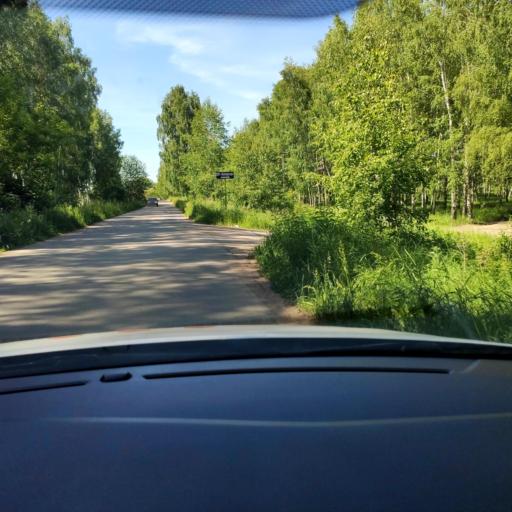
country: RU
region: Tatarstan
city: Staroye Arakchino
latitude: 55.8896
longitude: 49.0324
